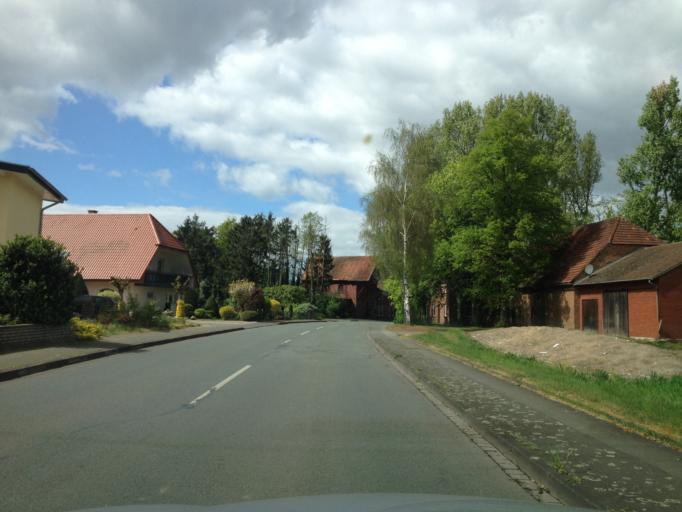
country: DE
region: North Rhine-Westphalia
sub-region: Regierungsbezirk Detmold
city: Delbruck
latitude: 51.8052
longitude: 8.5236
